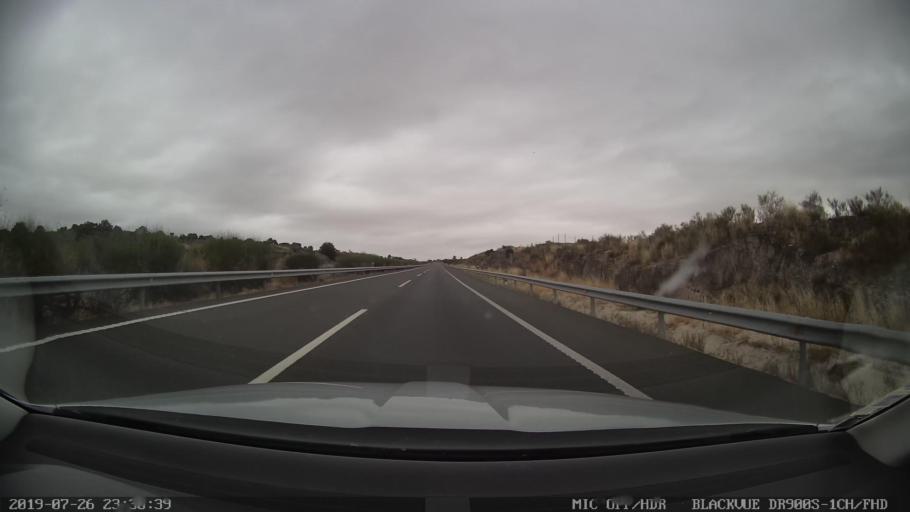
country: ES
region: Extremadura
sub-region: Provincia de Caceres
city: Trujillo
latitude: 39.4345
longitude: -5.8770
